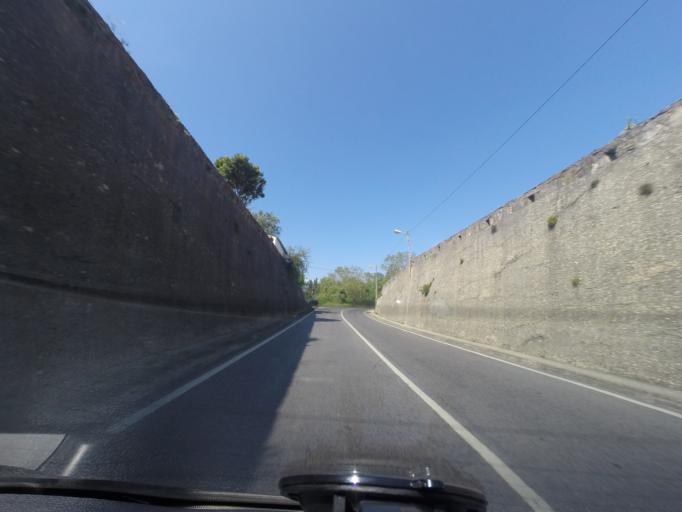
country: PT
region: Lisbon
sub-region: Sintra
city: Sintra
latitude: 38.8098
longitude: -9.3727
